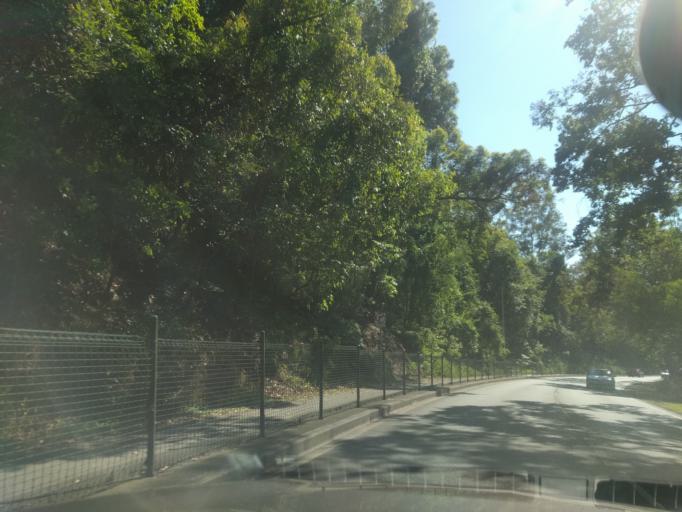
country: AU
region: Queensland
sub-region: Brisbane
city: Stafford
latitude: -27.4136
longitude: 153.0035
